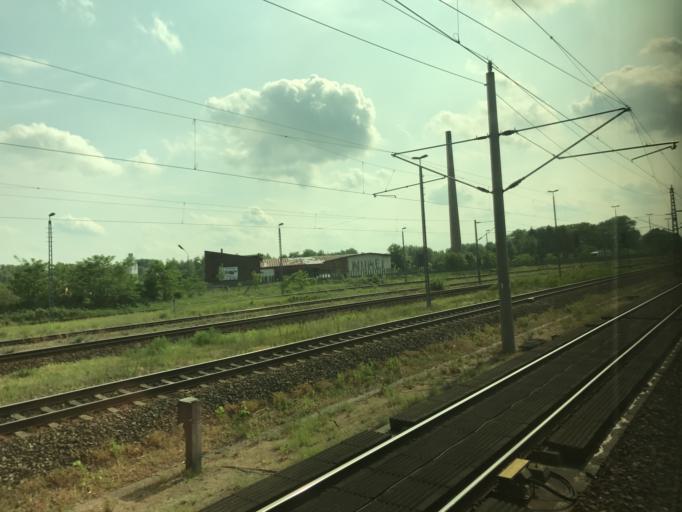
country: DE
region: Brandenburg
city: Rathenow
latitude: 52.5993
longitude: 12.3512
